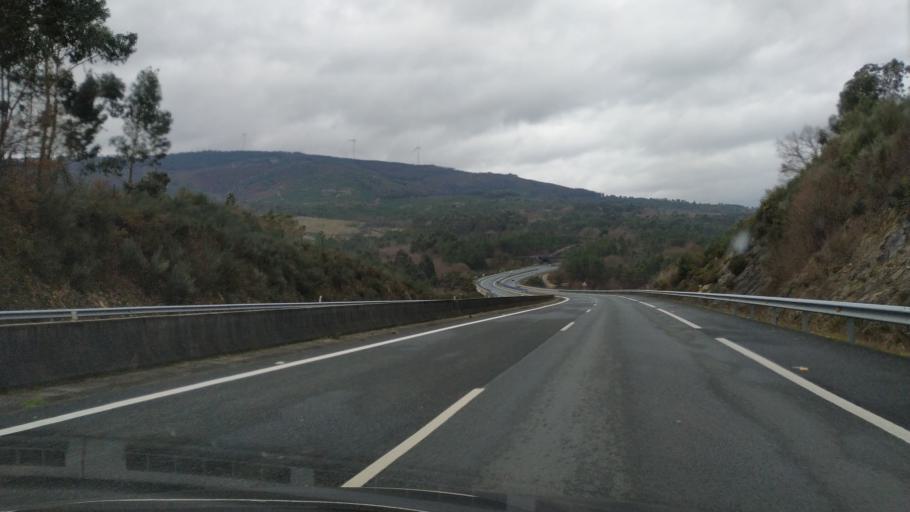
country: ES
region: Galicia
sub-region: Provincia de Ourense
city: Pinor
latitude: 42.4922
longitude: -8.0249
